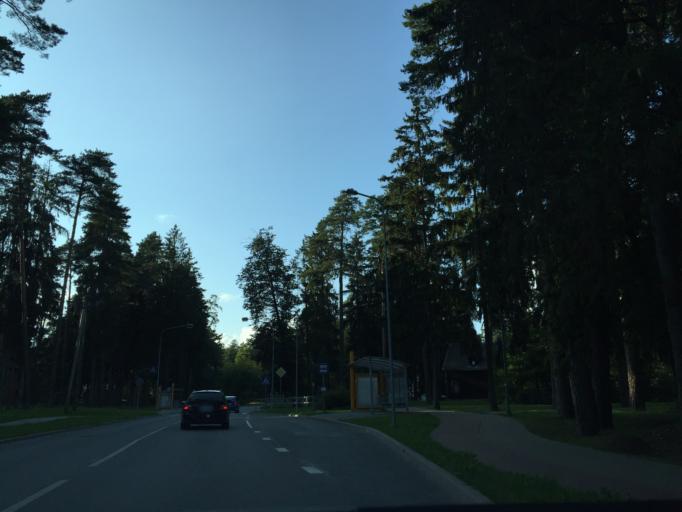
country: LV
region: Ogre
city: Ogre
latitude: 56.8184
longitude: 24.6162
